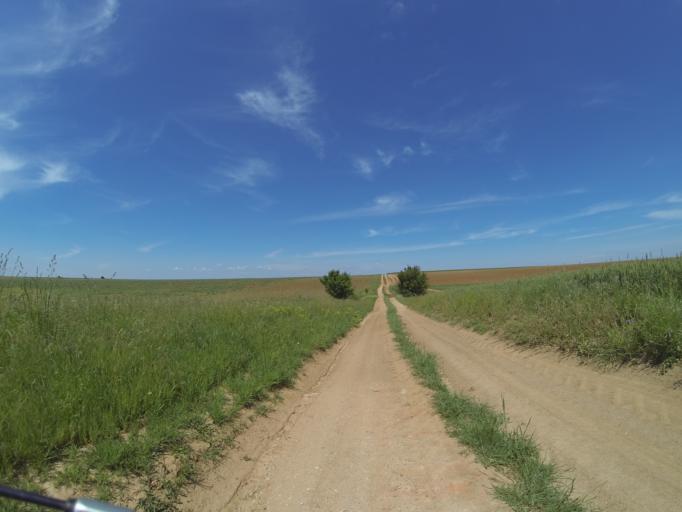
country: RO
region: Dolj
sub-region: Comuna Teslui
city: Teslui
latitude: 44.1851
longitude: 24.1719
